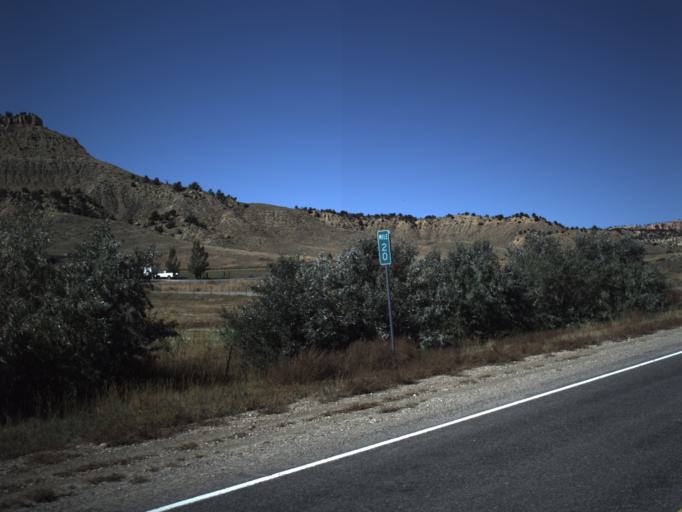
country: US
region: Utah
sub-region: Garfield County
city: Panguitch
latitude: 37.6395
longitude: -112.0818
